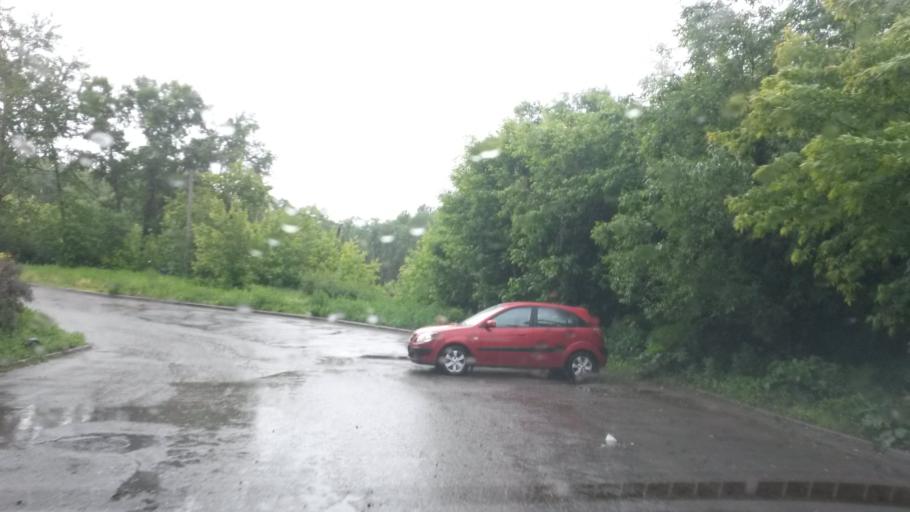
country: RU
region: Jaroslavl
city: Yaroslavl
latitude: 57.5904
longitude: 39.8410
